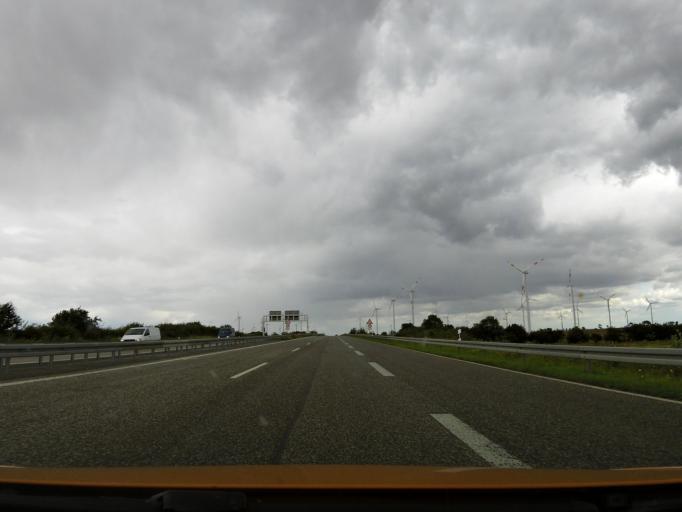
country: DE
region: Brandenburg
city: Gramzow
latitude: 53.2485
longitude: 14.0165
